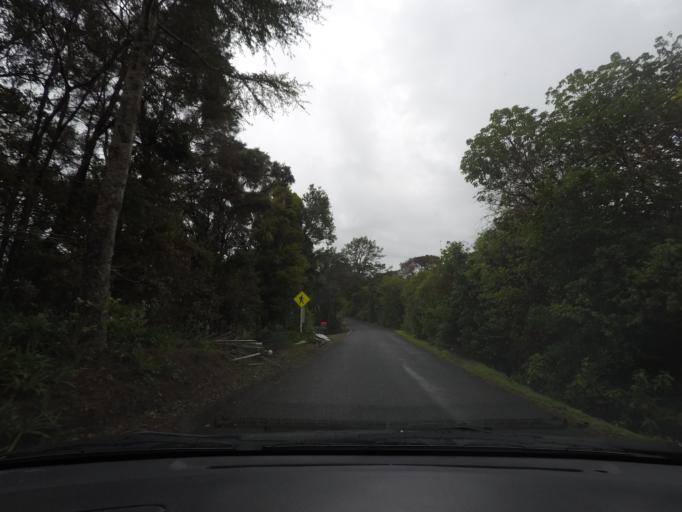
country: NZ
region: Auckland
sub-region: Auckland
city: Warkworth
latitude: -36.4767
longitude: 174.7320
